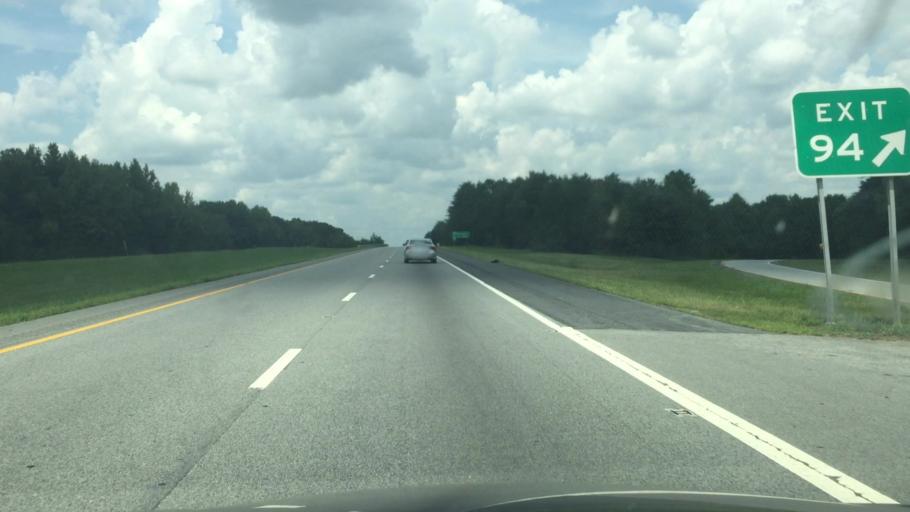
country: US
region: North Carolina
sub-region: Guilford County
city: Pleasant Garden
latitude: 35.9848
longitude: -79.8243
